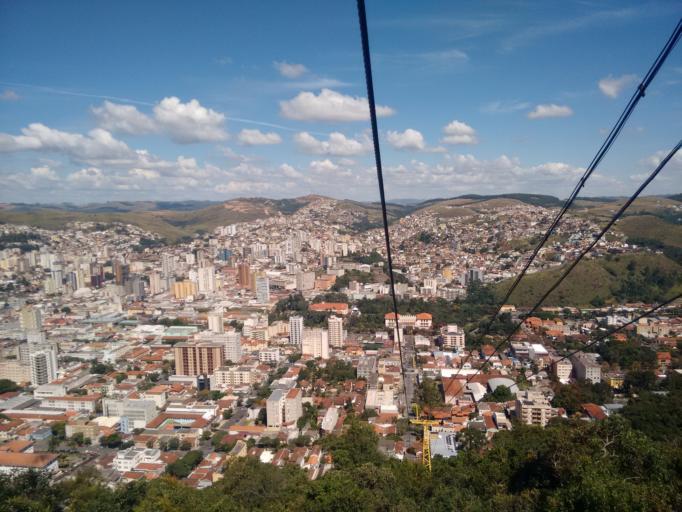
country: BR
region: Minas Gerais
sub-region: Pocos De Caldas
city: Pocos de Caldas
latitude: -21.7778
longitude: -46.5689
